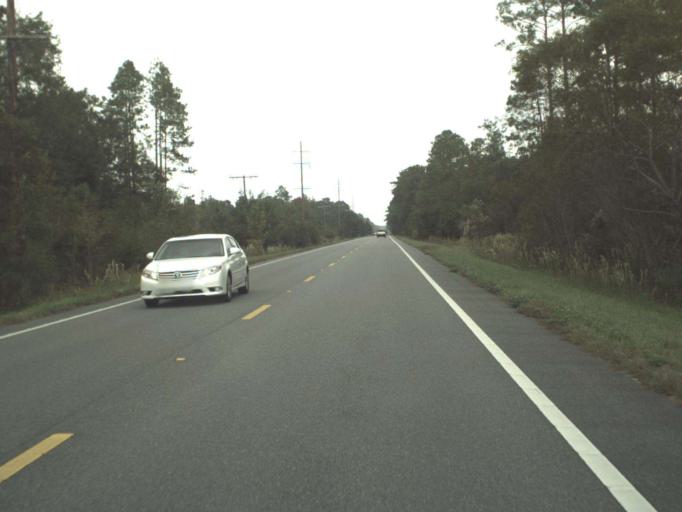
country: US
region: Florida
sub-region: Wakulla County
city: Crawfordville
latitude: 30.0132
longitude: -84.5017
